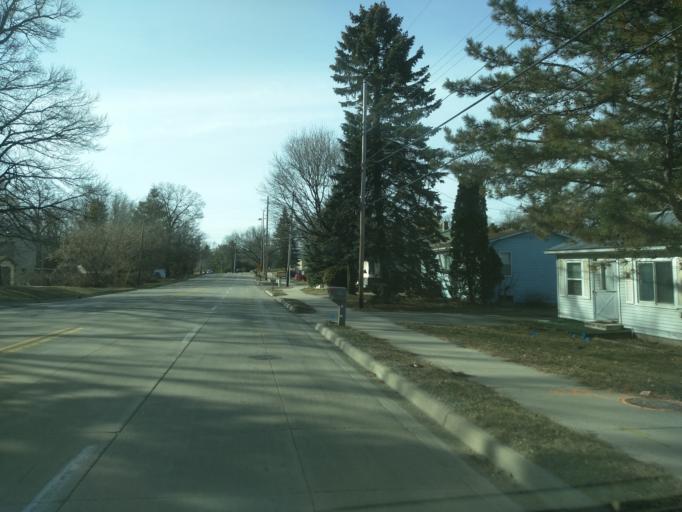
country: US
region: Michigan
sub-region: Ingham County
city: Haslett
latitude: 42.7646
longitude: -84.4130
